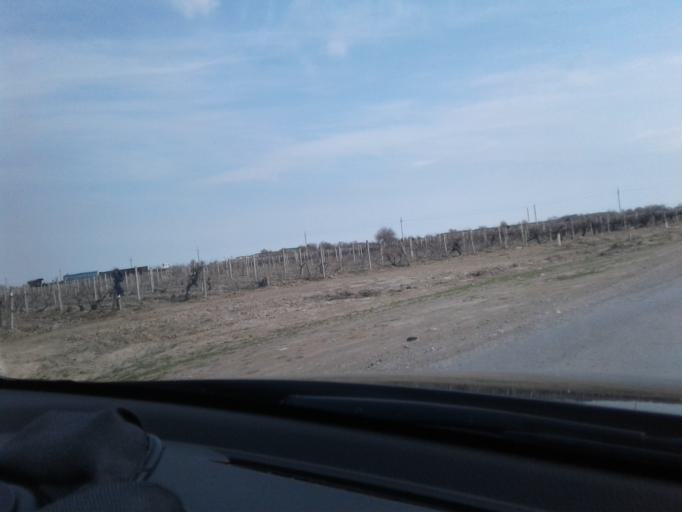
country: TM
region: Ahal
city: Ashgabat
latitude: 38.1170
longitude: 58.3584
